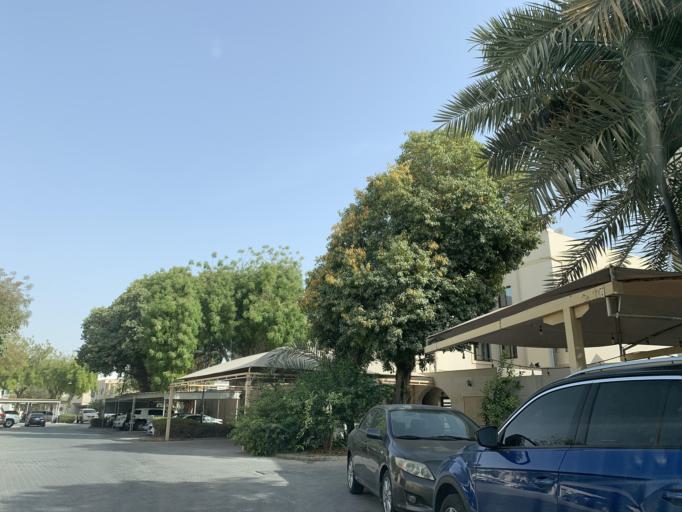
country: BH
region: Northern
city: Madinat `Isa
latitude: 26.1746
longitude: 50.5371
